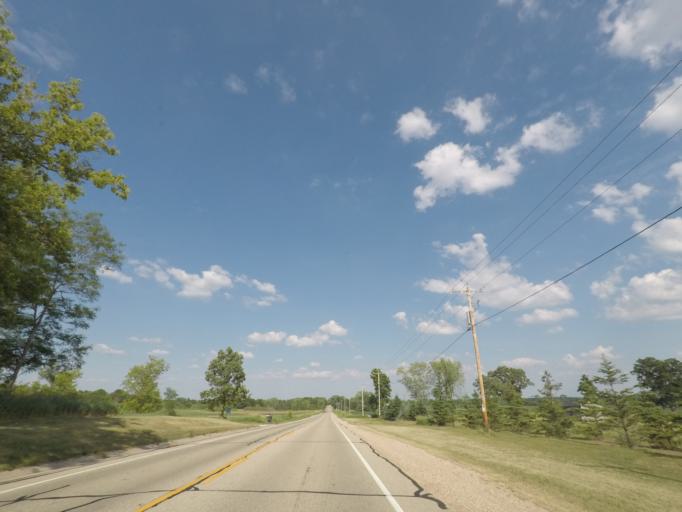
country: US
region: Wisconsin
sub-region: Walworth County
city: East Troy
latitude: 42.7931
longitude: -88.4858
